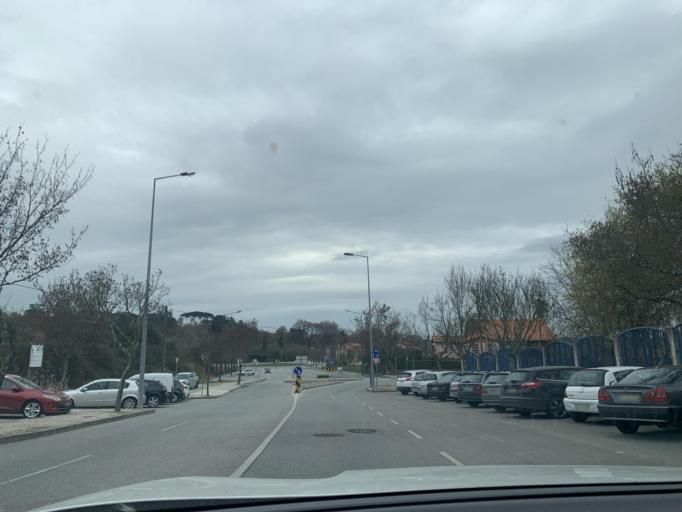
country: PT
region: Viseu
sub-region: Viseu
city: Viseu
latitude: 40.6503
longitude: -7.9035
